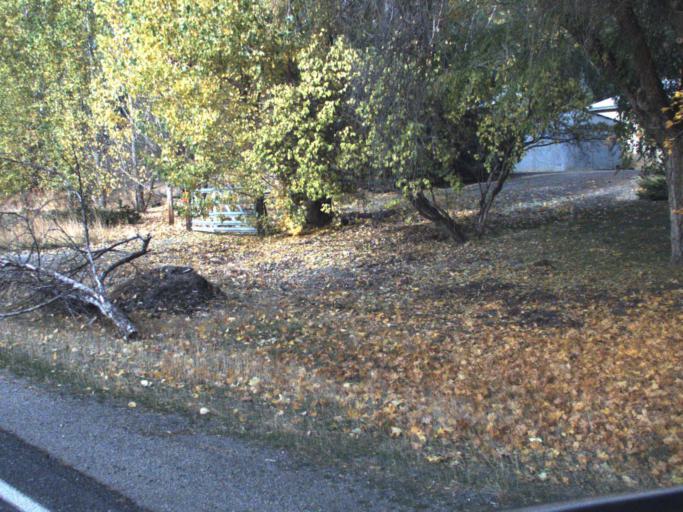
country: US
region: Washington
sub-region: Stevens County
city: Kettle Falls
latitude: 48.7080
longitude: -118.0208
